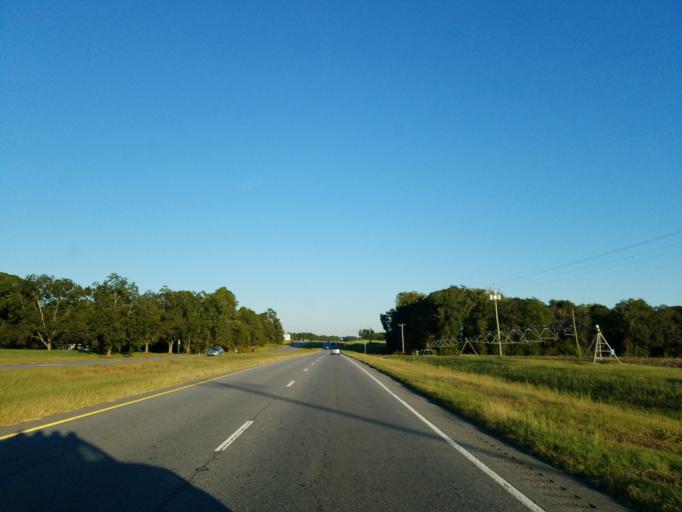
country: US
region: Georgia
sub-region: Worth County
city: Sylvester
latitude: 31.4794
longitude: -83.6834
